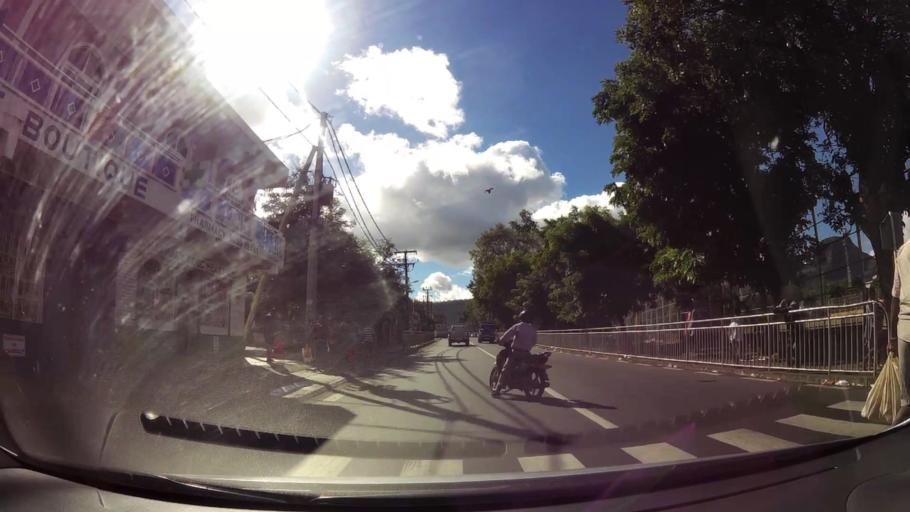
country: MU
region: Pamplemousses
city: Le Hochet
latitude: -20.1476
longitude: 57.5210
